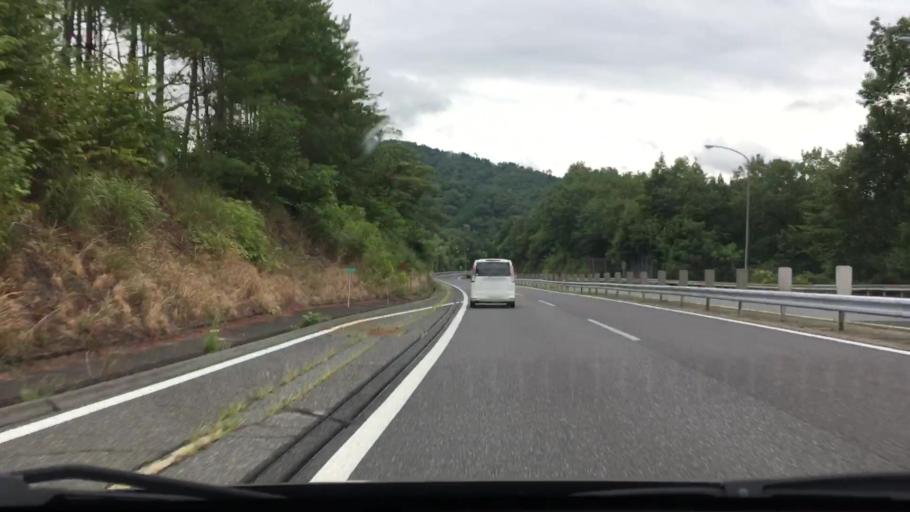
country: JP
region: Hiroshima
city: Hiroshima-shi
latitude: 34.6830
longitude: 132.5615
